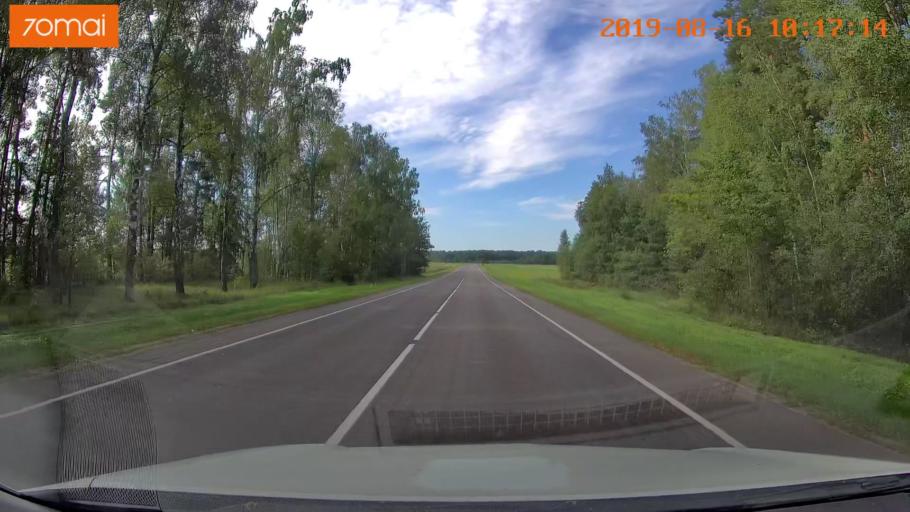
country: BY
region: Mogilev
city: Asipovichy
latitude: 53.3134
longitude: 28.7139
